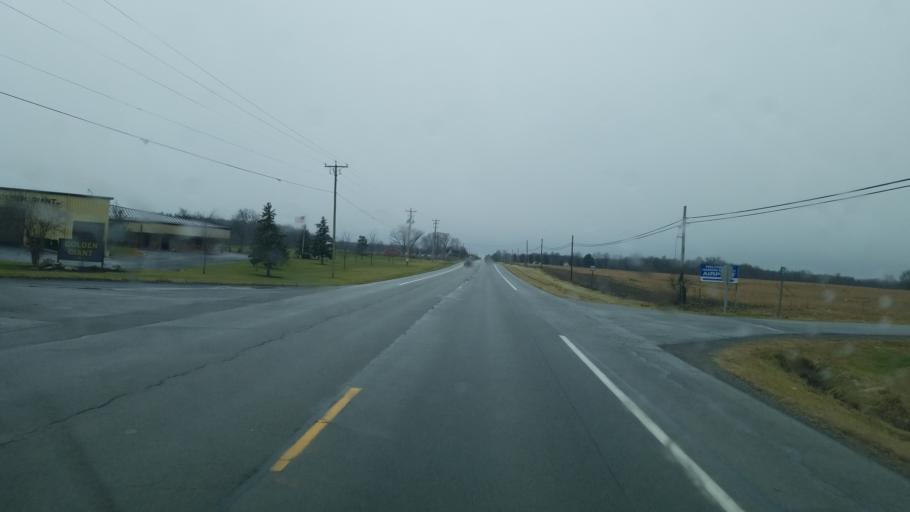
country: US
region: Ohio
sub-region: Hardin County
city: Kenton
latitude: 40.6133
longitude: -83.6275
